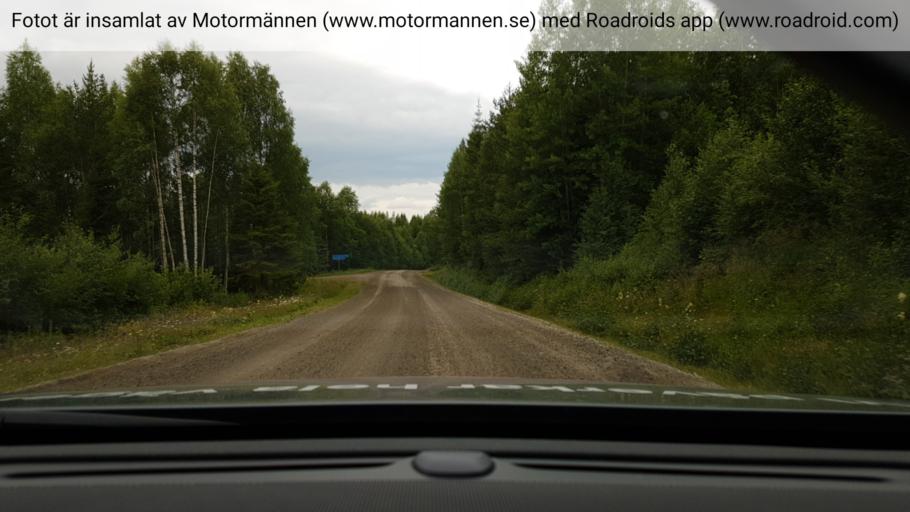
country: SE
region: Vaesterbotten
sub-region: Vannas Kommun
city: Vannasby
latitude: 64.0911
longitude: 20.0306
